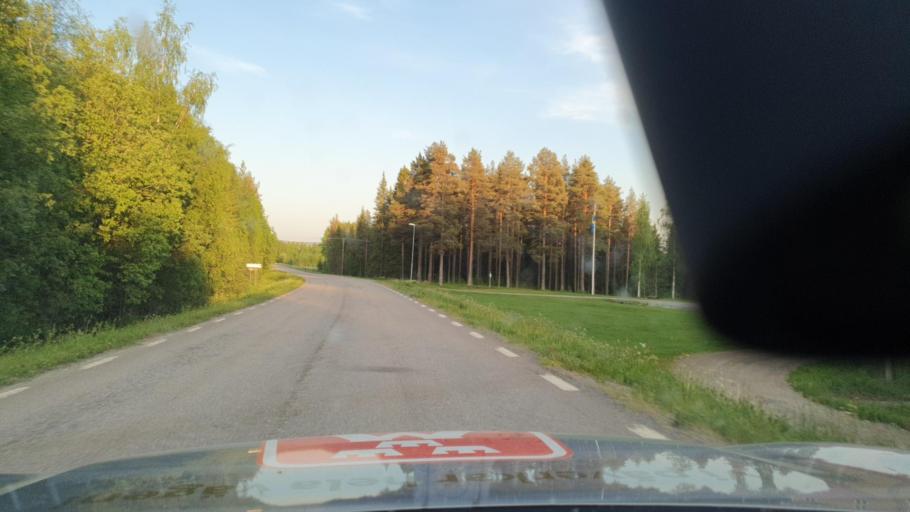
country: SE
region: Norrbotten
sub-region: Bodens Kommun
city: Boden
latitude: 66.0482
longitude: 21.7864
